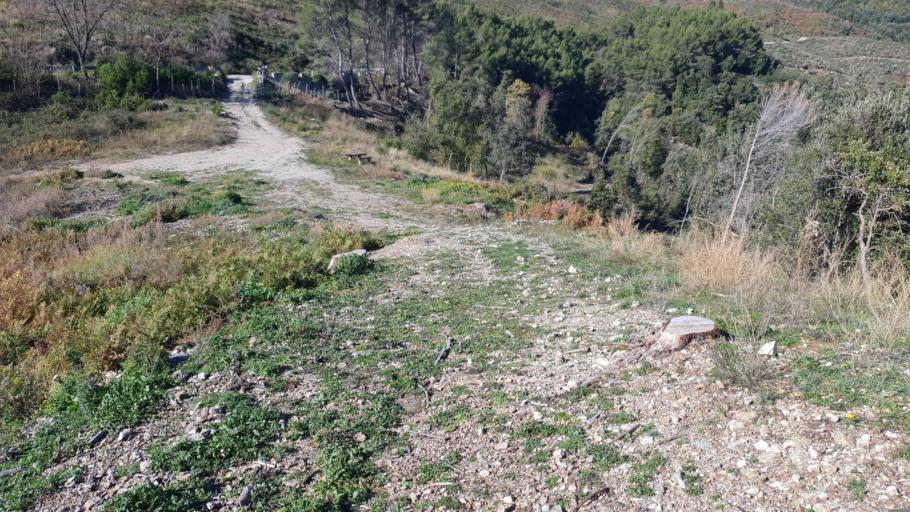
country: IT
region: Calabria
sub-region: Provincia di Catanzaro
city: Zagarise
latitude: 39.0119
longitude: 16.6850
